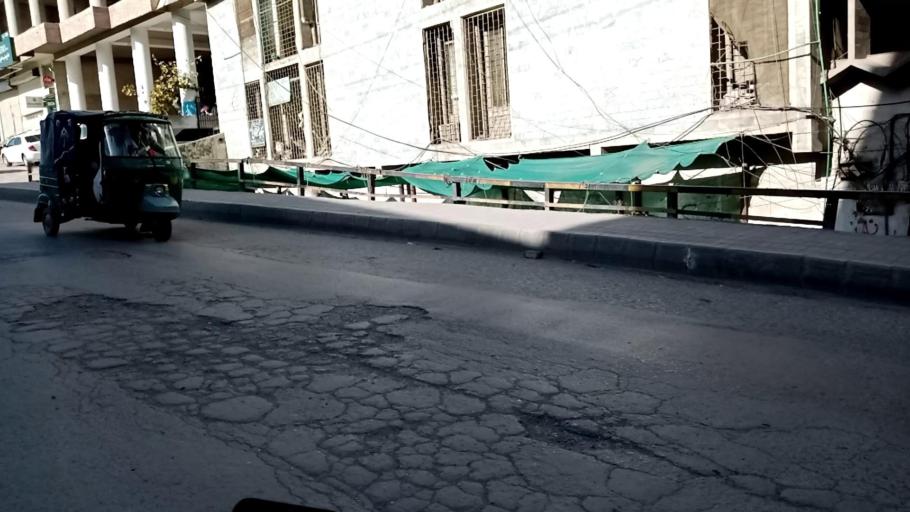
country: PK
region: Khyber Pakhtunkhwa
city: Peshawar
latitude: 34.0089
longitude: 71.5632
